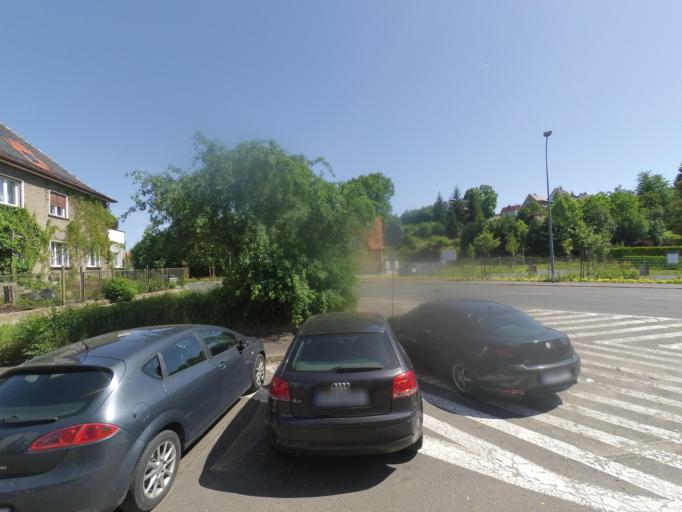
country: PL
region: Lower Silesian Voivodeship
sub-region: Powiat walbrzyski
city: Walbrzych
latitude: 50.7591
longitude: 16.2854
